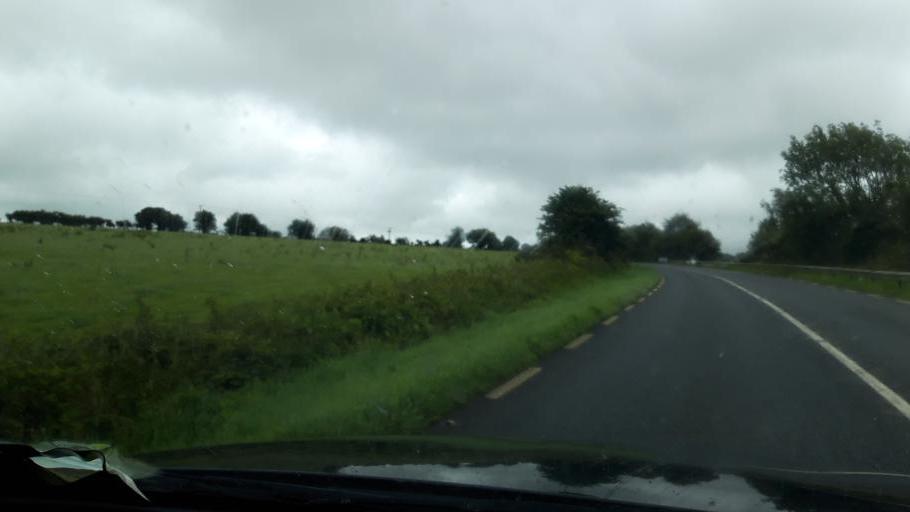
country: IE
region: Leinster
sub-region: Loch Garman
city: New Ross
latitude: 52.4294
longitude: -6.8105
